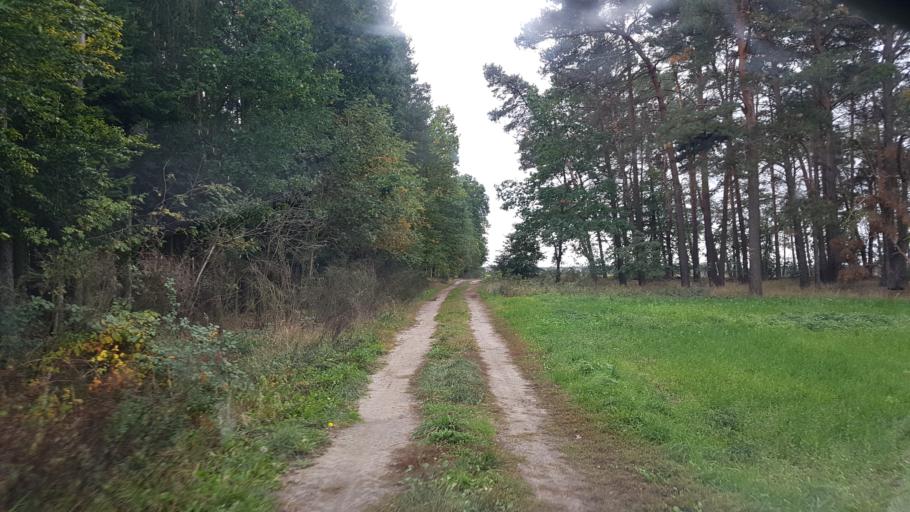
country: DE
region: Brandenburg
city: Finsterwalde
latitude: 51.5778
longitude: 13.6720
